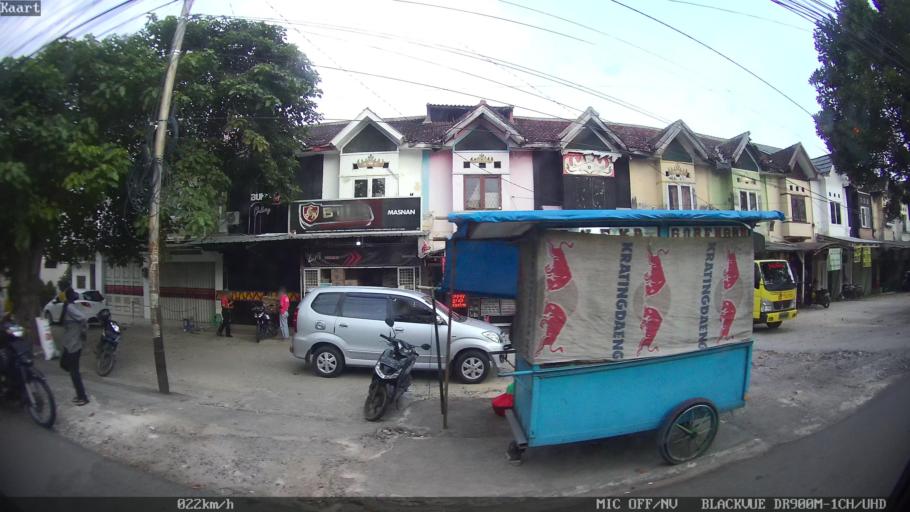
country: ID
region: Lampung
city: Kedaton
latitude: -5.4001
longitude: 105.2114
